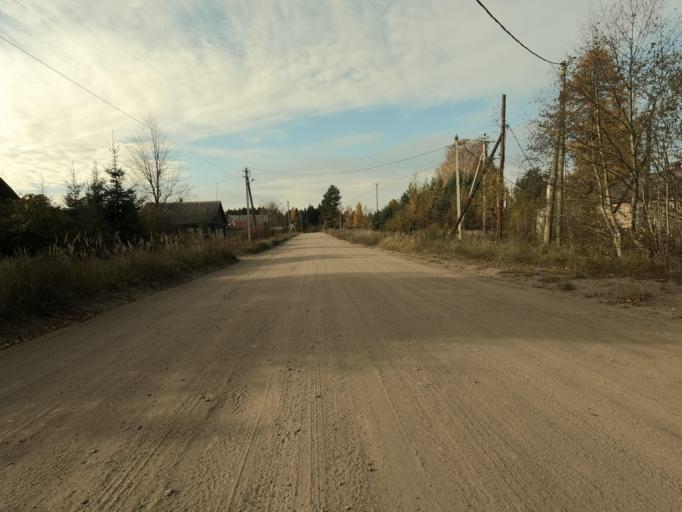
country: RU
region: Leningrad
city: Priladozhskiy
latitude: 59.6302
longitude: 31.4015
